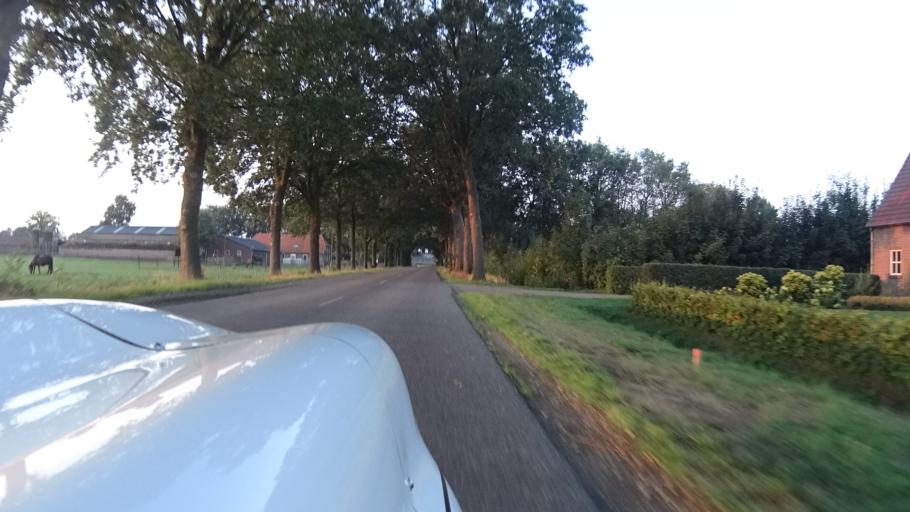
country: NL
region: North Brabant
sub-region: Gemeente Mill en Sint Hubert
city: Wilbertoord
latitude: 51.6061
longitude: 5.7838
